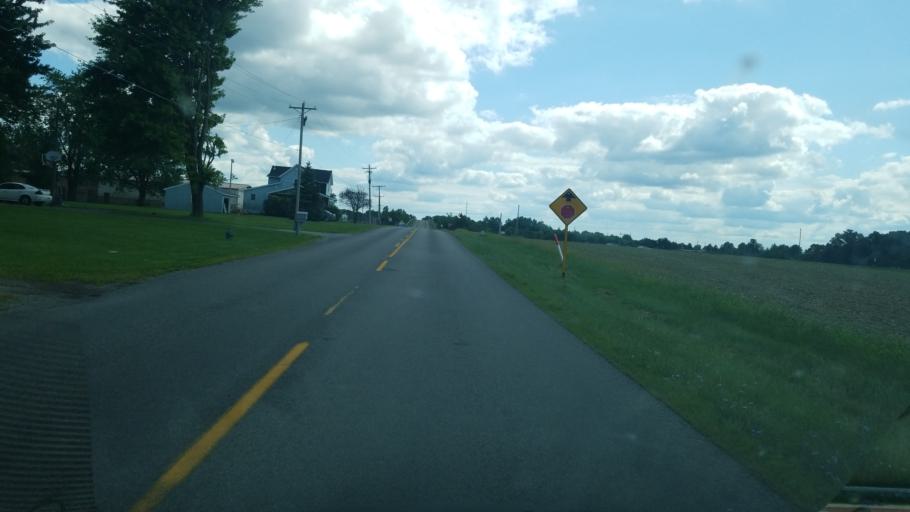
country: US
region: Ohio
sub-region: Allen County
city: Lima
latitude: 40.7763
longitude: -84.0706
